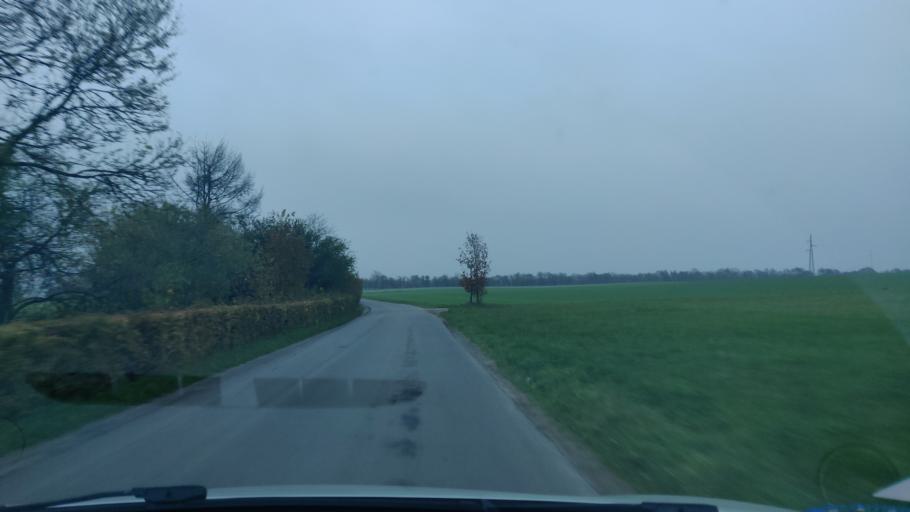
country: DK
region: South Denmark
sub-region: Kolding Kommune
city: Kolding
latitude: 55.5768
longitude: 9.4759
